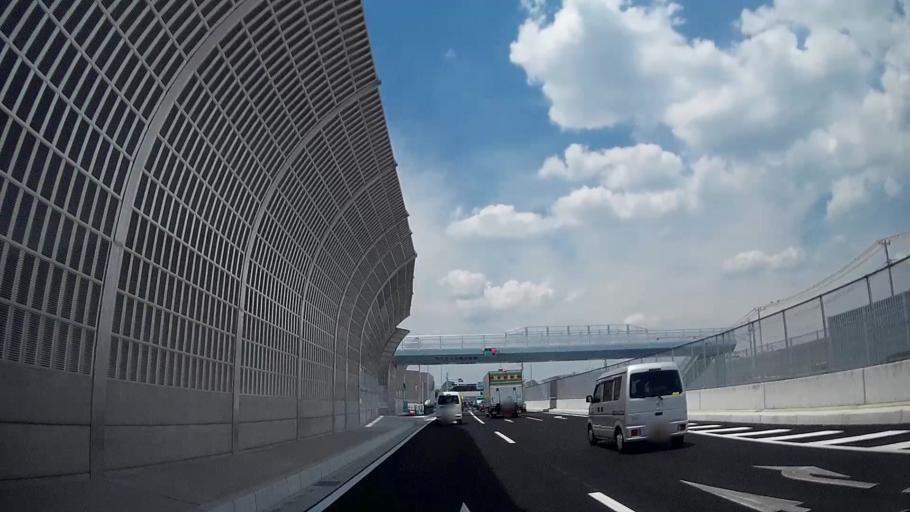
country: JP
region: Chiba
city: Matsudo
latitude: 35.7430
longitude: 139.9198
